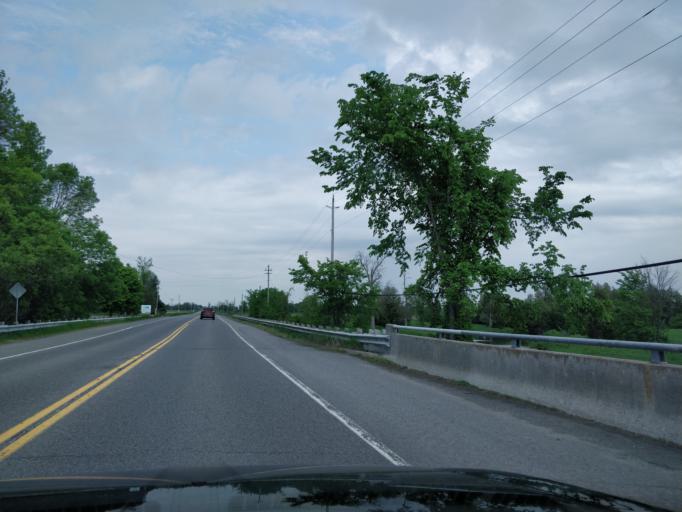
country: CA
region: Ontario
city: Bells Corners
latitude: 45.1350
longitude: -75.9327
